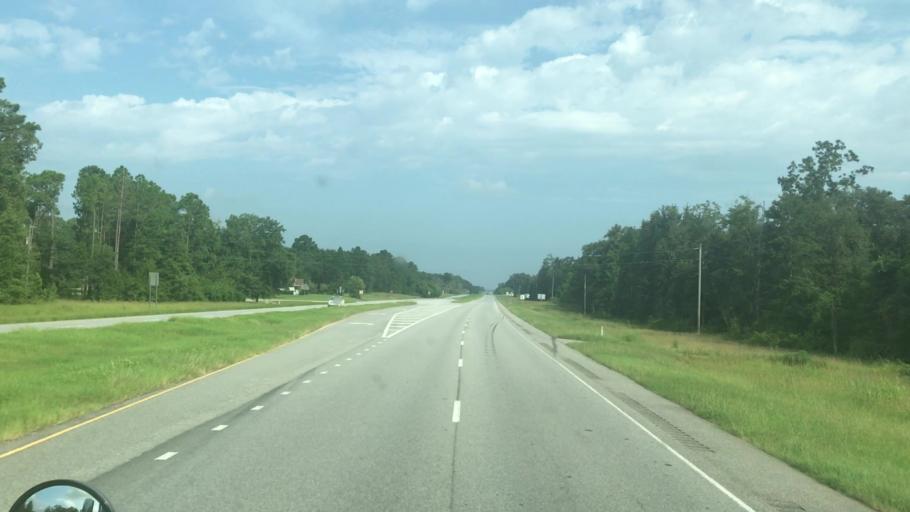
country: US
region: Georgia
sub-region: Early County
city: Blakely
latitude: 31.2877
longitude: -84.8454
